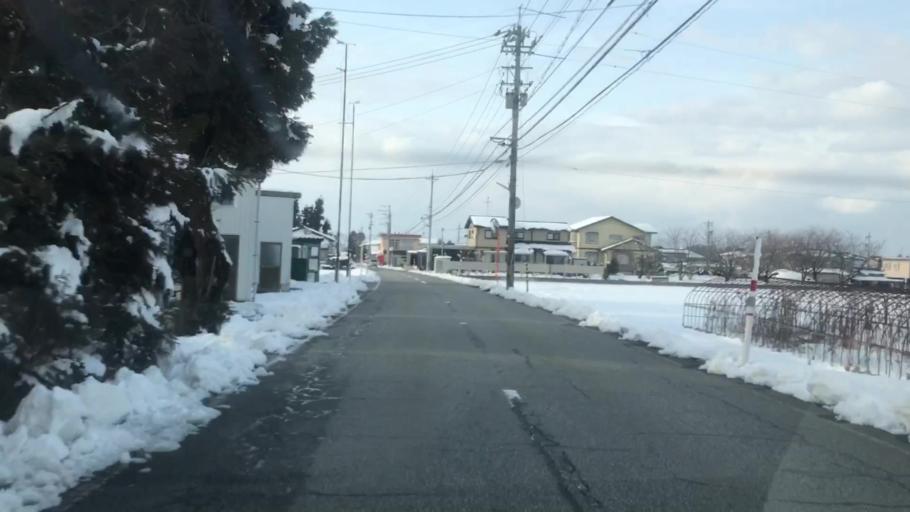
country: JP
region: Toyama
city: Toyama-shi
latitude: 36.6227
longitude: 137.2817
